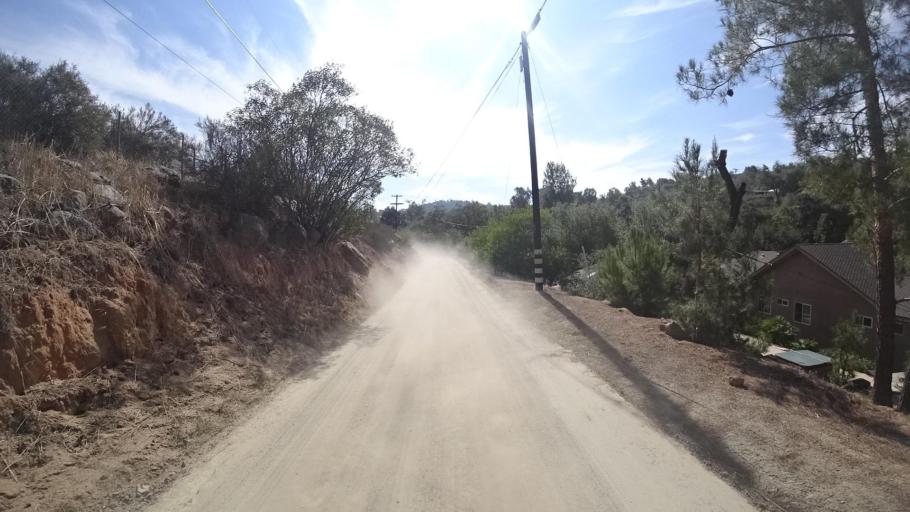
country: US
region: California
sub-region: San Diego County
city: Alpine
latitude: 32.8374
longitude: -116.7992
